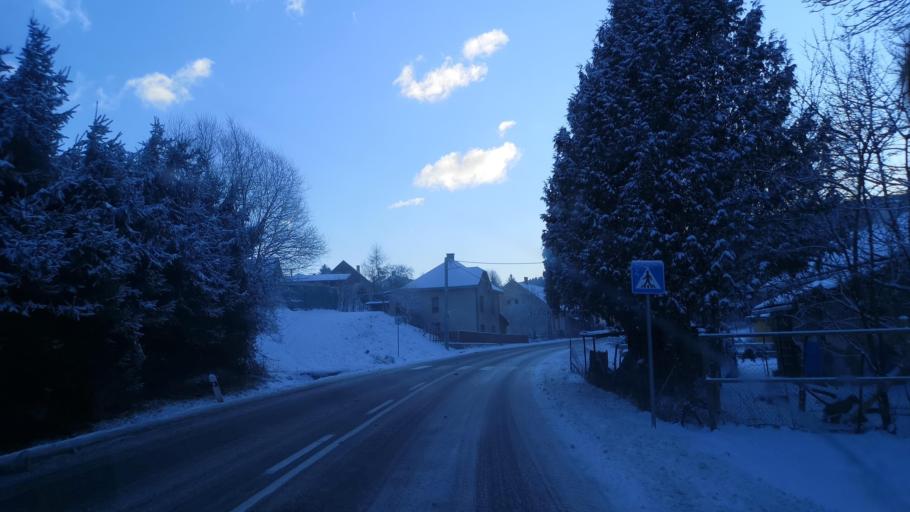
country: SK
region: Banskobystricky
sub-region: Okres Banska Bystrica
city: Brezno
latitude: 48.8289
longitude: 19.7611
